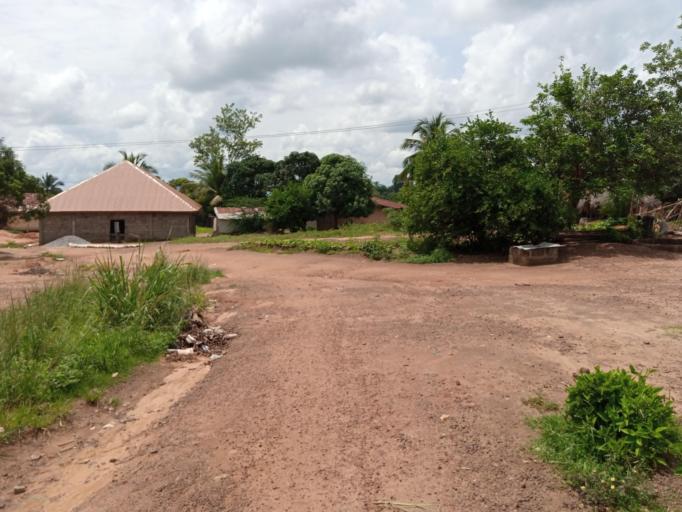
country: SL
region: Southern Province
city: Bo
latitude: 7.9419
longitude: -11.7205
